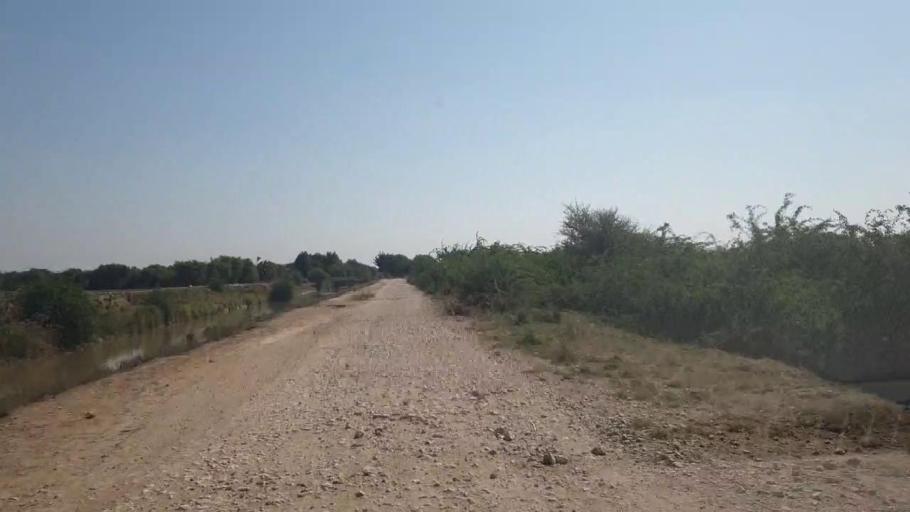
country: PK
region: Sindh
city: Digri
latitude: 24.9416
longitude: 69.1595
